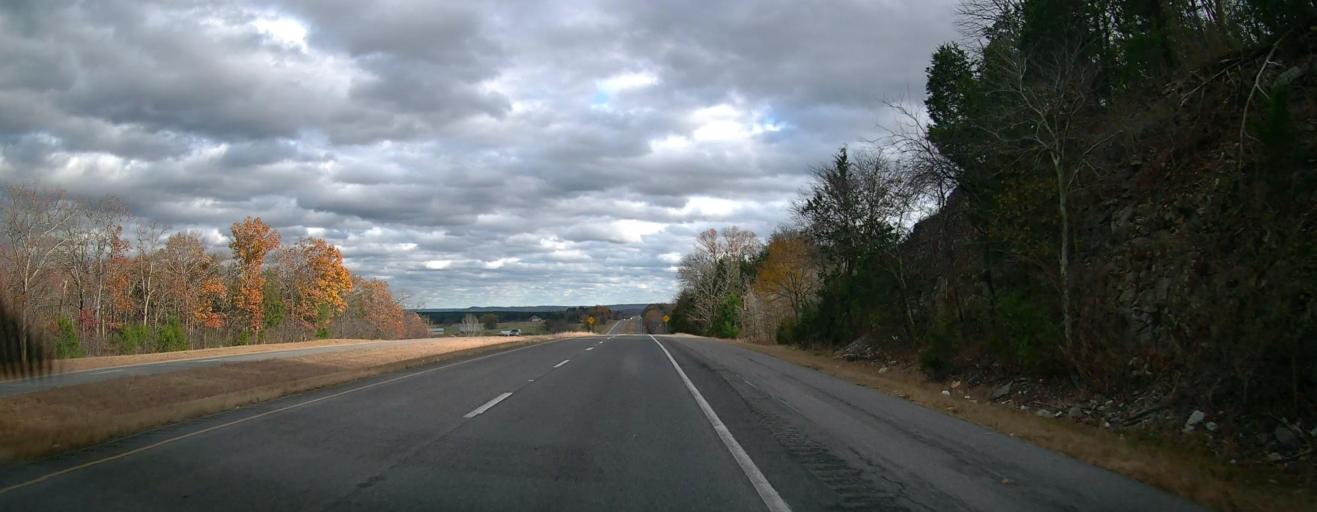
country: US
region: Alabama
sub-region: Morgan County
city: Danville
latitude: 34.3971
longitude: -87.1259
